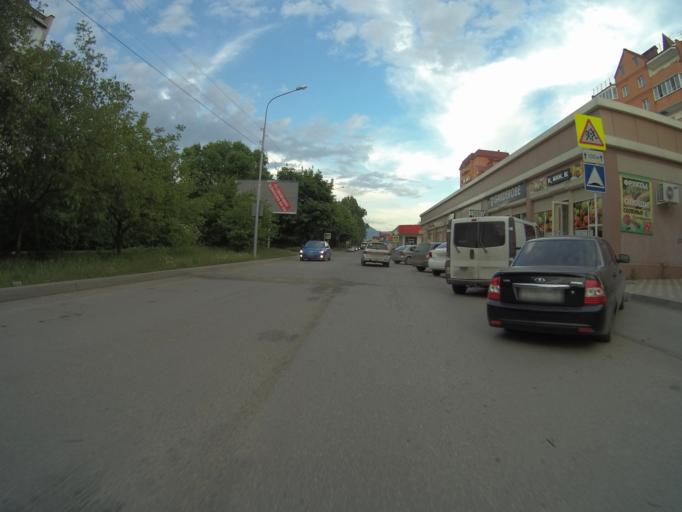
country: RU
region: Stavropol'skiy
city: Yessentukskaya
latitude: 44.0453
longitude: 42.8926
